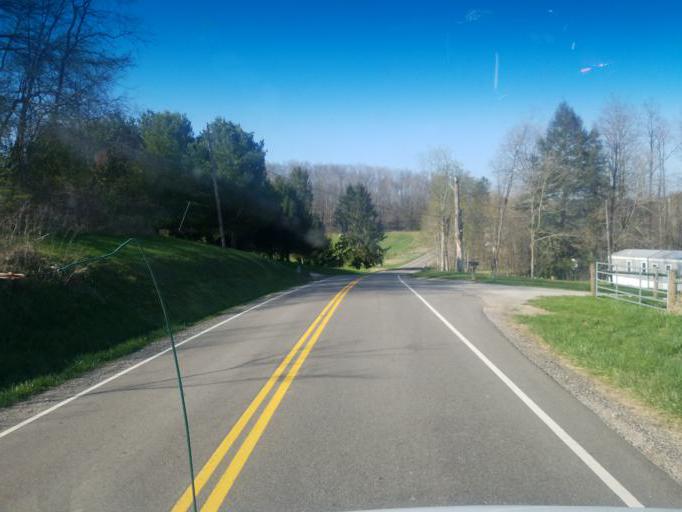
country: US
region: Ohio
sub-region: Knox County
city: Oak Hill
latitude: 40.3289
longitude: -82.0743
